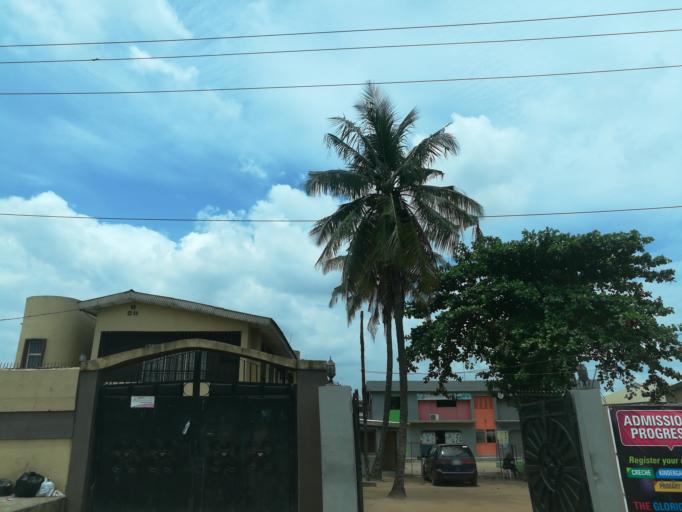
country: NG
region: Lagos
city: Ebute Ikorodu
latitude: 6.6005
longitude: 3.4936
